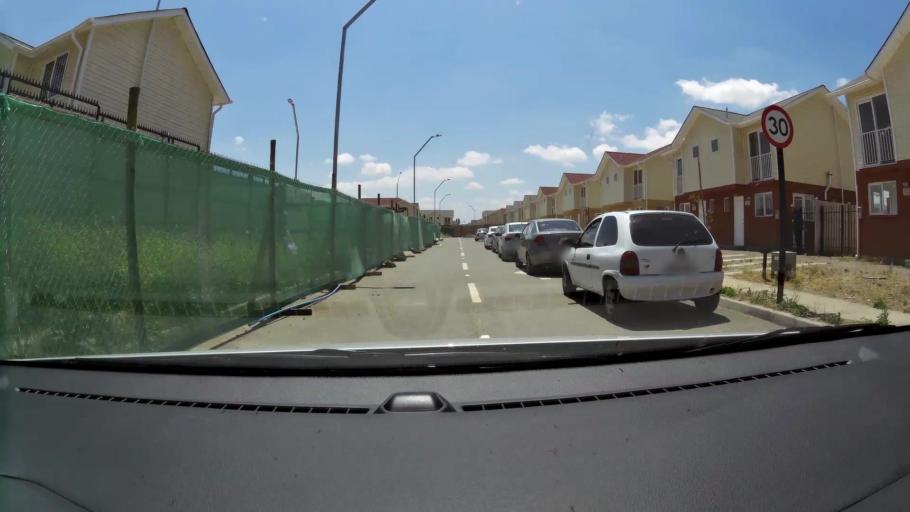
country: CL
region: Santiago Metropolitan
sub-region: Provincia de Talagante
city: Penaflor
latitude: -33.5736
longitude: -70.7955
